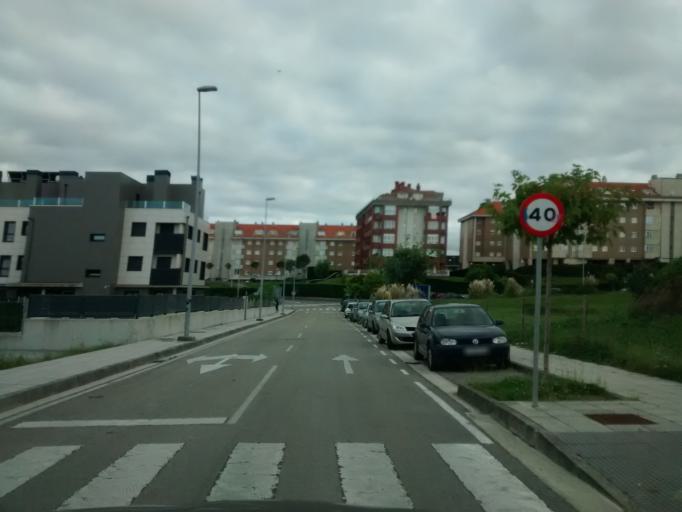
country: ES
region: Cantabria
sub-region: Provincia de Cantabria
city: Santander
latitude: 43.4809
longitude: -3.8005
